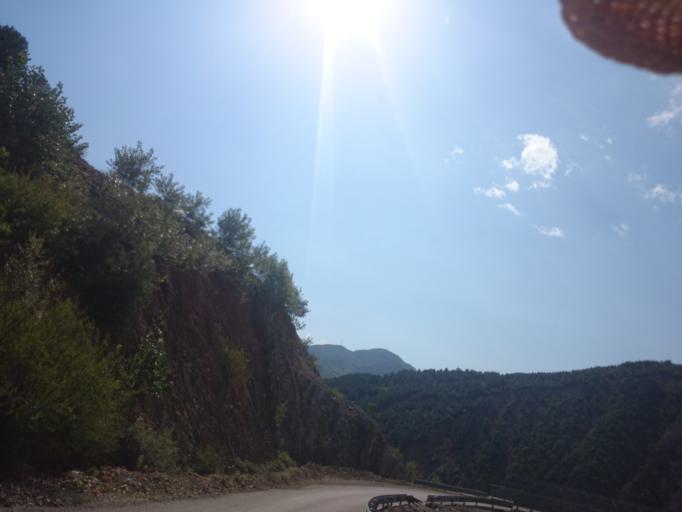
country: AL
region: Lezhe
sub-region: Rrethi i Lezhes
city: Blinisht
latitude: 41.8681
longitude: 20.0261
